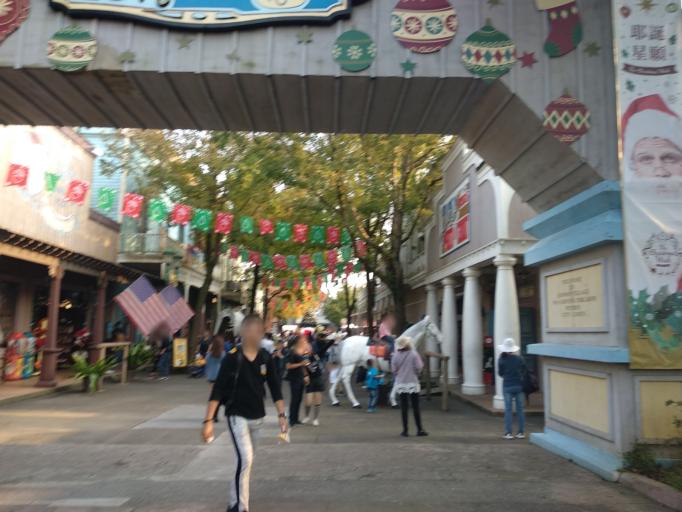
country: TW
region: Taiwan
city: Daxi
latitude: 24.8206
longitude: 121.1822
